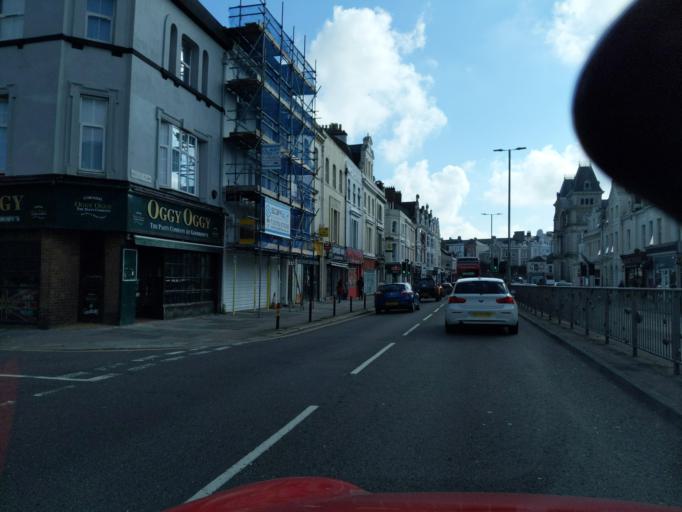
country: GB
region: England
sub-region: Plymouth
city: Plymouth
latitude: 50.3821
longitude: -4.1338
